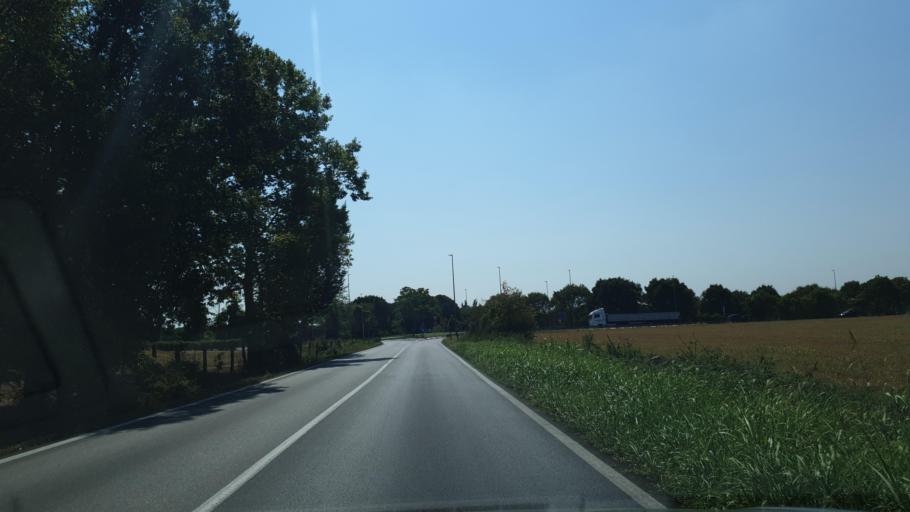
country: IT
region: Lombardy
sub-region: Provincia di Brescia
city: Carzago Riviera
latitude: 45.5079
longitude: 10.4638
